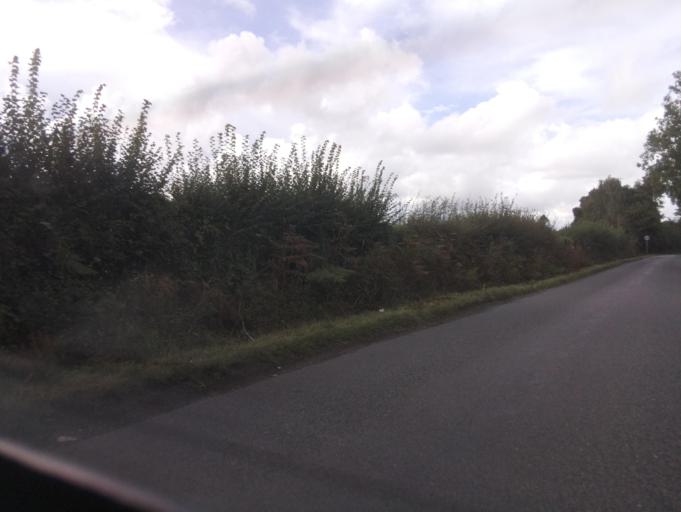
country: GB
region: England
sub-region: Worcestershire
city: Kidderminster
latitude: 52.3626
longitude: -2.1926
